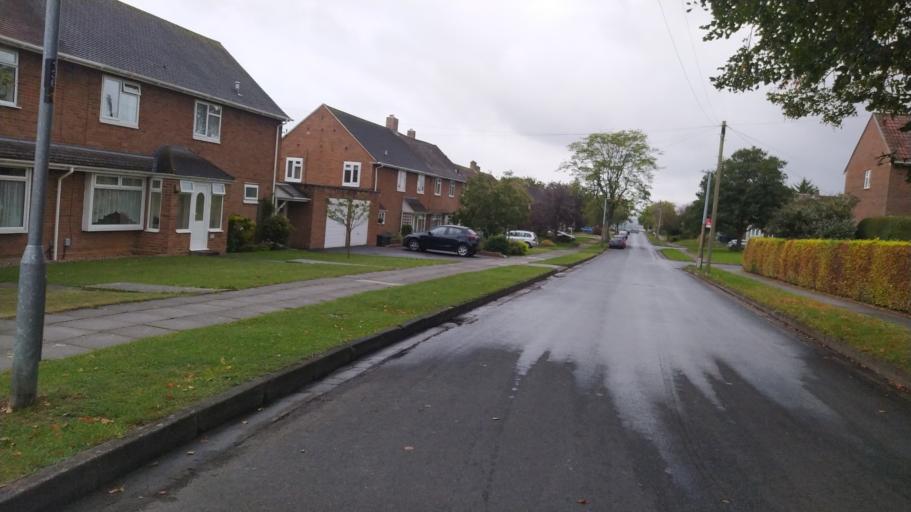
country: GB
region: England
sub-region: Wiltshire
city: Salisbury
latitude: 51.0883
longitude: -1.7927
